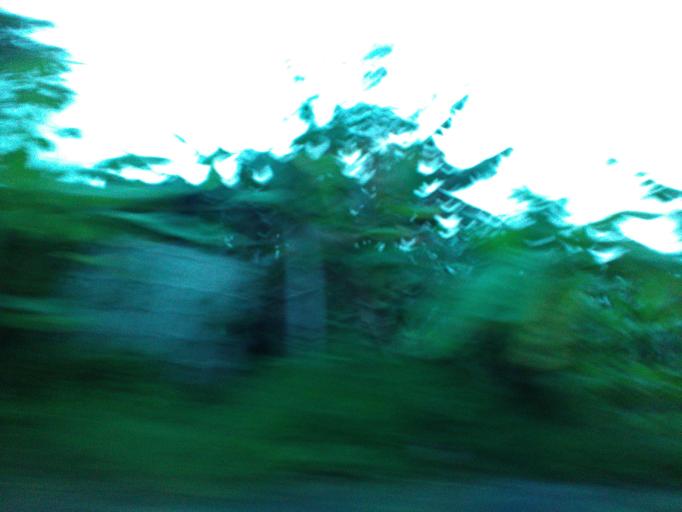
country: ID
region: Central Java
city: Ceper
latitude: -7.6550
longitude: 110.6755
